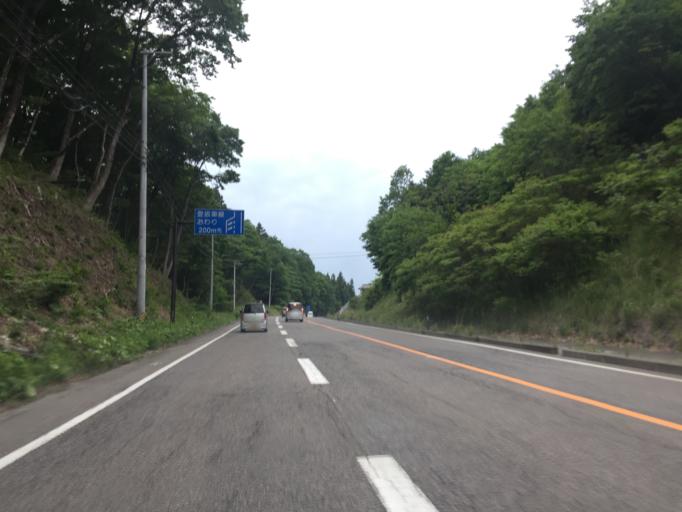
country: JP
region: Fukushima
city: Namie
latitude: 37.4320
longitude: 140.8049
